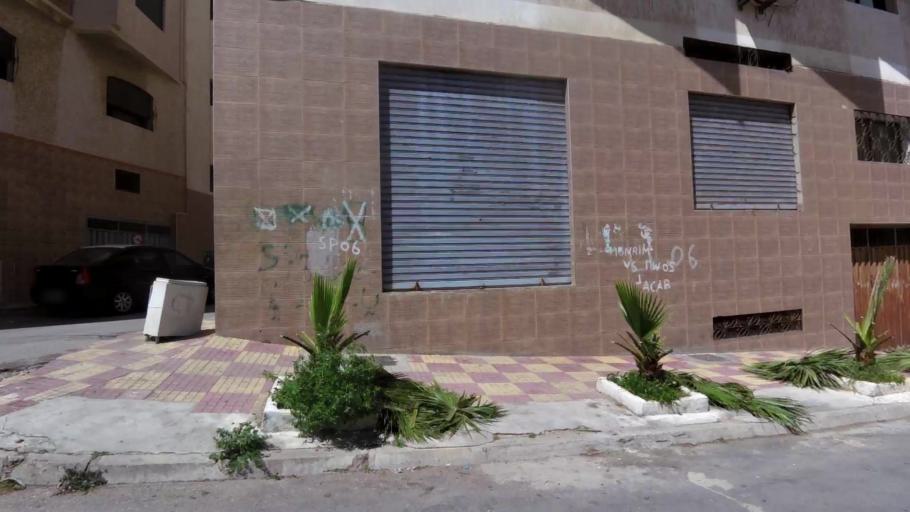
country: MA
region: Tanger-Tetouan
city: Tetouan
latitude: 35.5758
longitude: -5.3506
